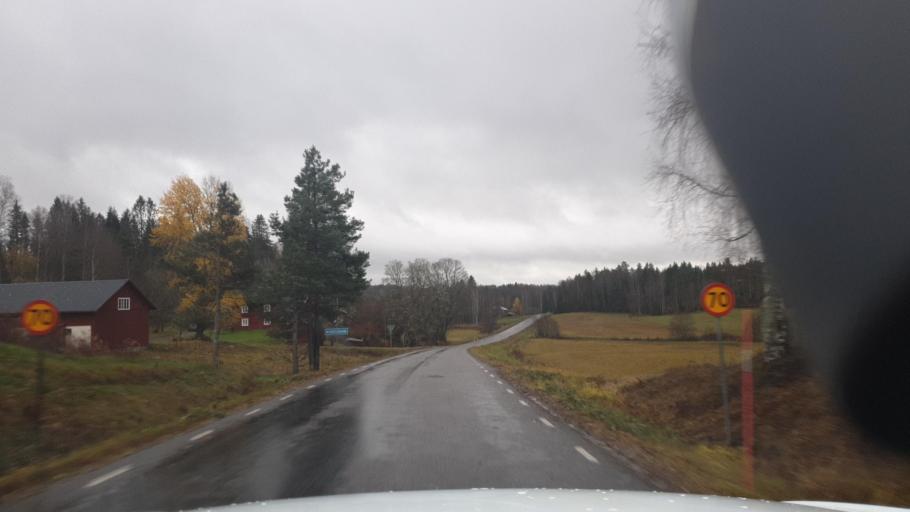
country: SE
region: Vaermland
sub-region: Eda Kommun
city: Charlottenberg
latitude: 59.8057
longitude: 12.1513
